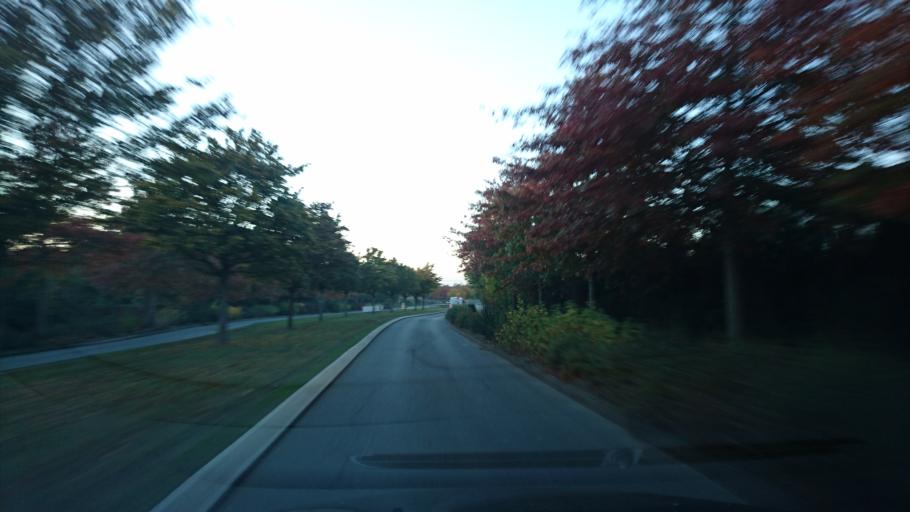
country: FR
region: Brittany
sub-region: Departement du Morbihan
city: Auray
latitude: 47.6805
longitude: -3.0140
